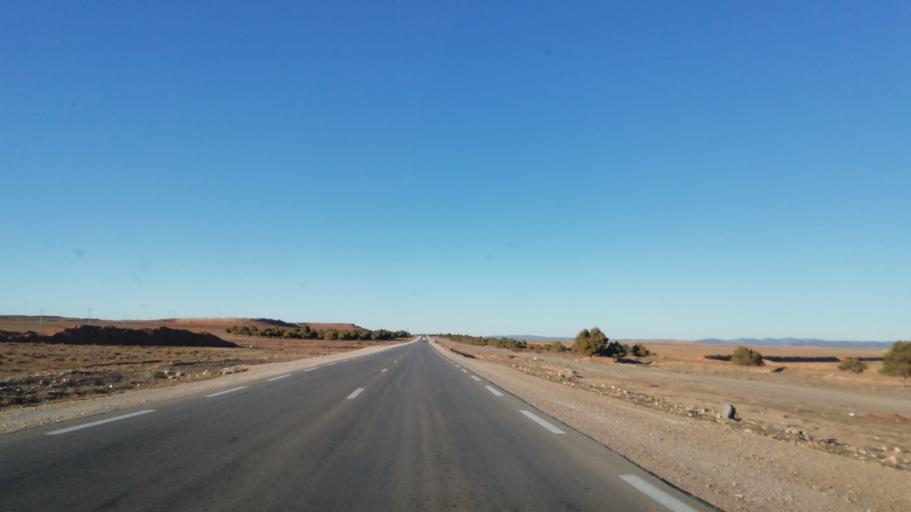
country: DZ
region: Tlemcen
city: Sebdou
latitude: 34.4926
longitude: -1.2746
